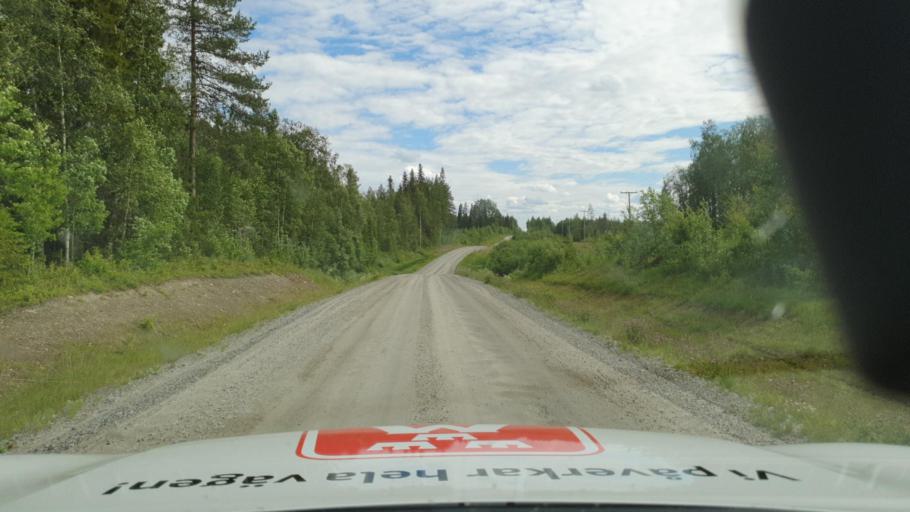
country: SE
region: Vaesterbotten
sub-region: Norsjo Kommun
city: Norsjoe
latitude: 64.8677
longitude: 19.4839
